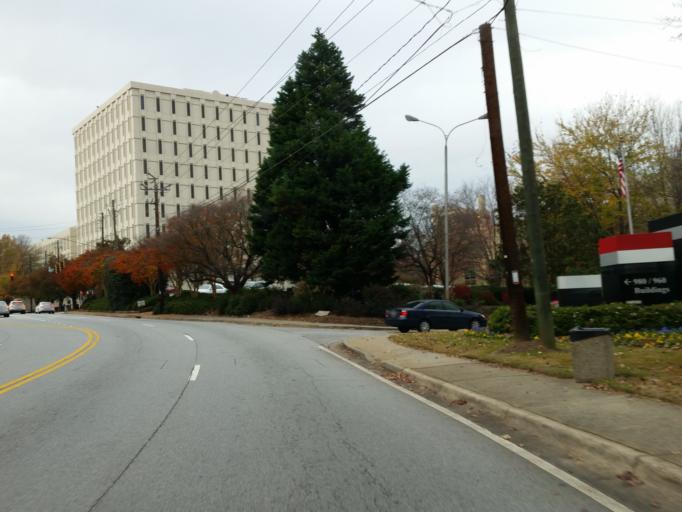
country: US
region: Georgia
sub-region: Fulton County
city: Sandy Springs
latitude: 33.9078
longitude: -84.3537
